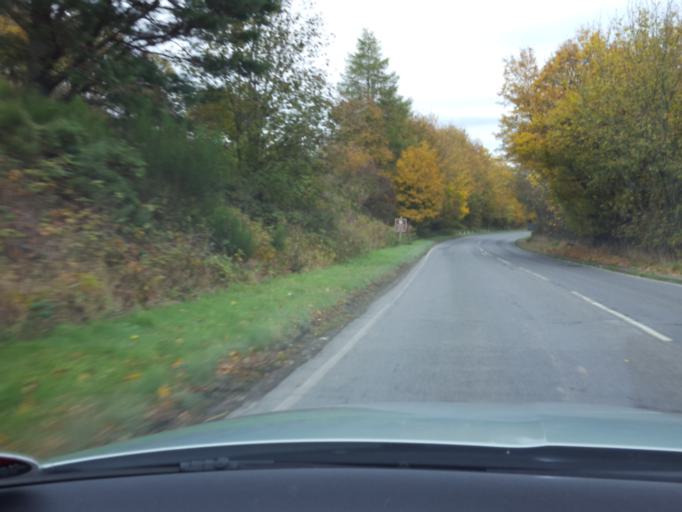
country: GB
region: Scotland
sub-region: The Scottish Borders
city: Peebles
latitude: 55.6527
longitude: -3.2143
